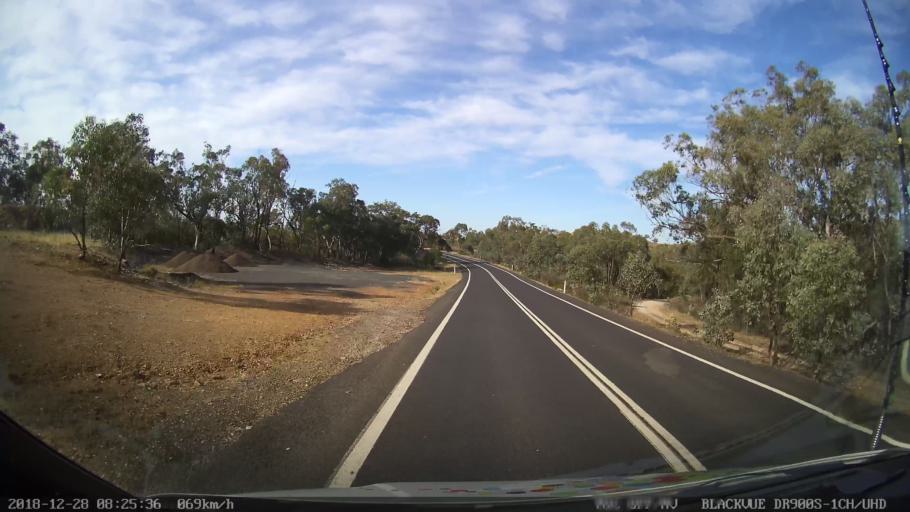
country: AU
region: New South Wales
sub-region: Blayney
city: Blayney
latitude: -33.9277
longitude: 149.3516
